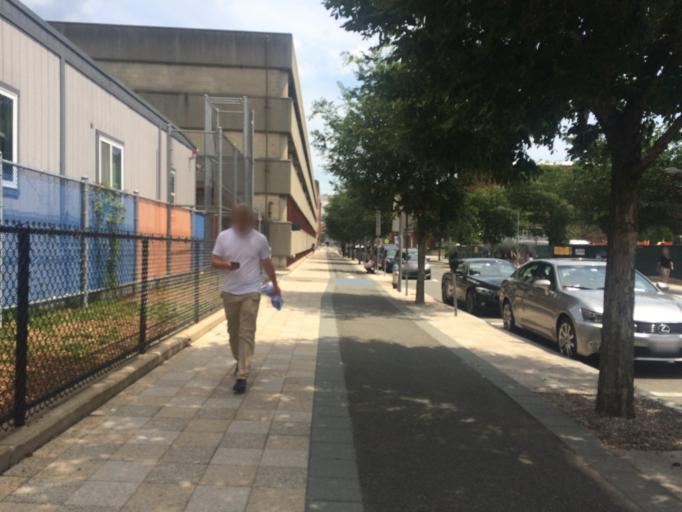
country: US
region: Massachusetts
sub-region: Middlesex County
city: Cambridge
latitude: 42.3584
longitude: -71.0986
